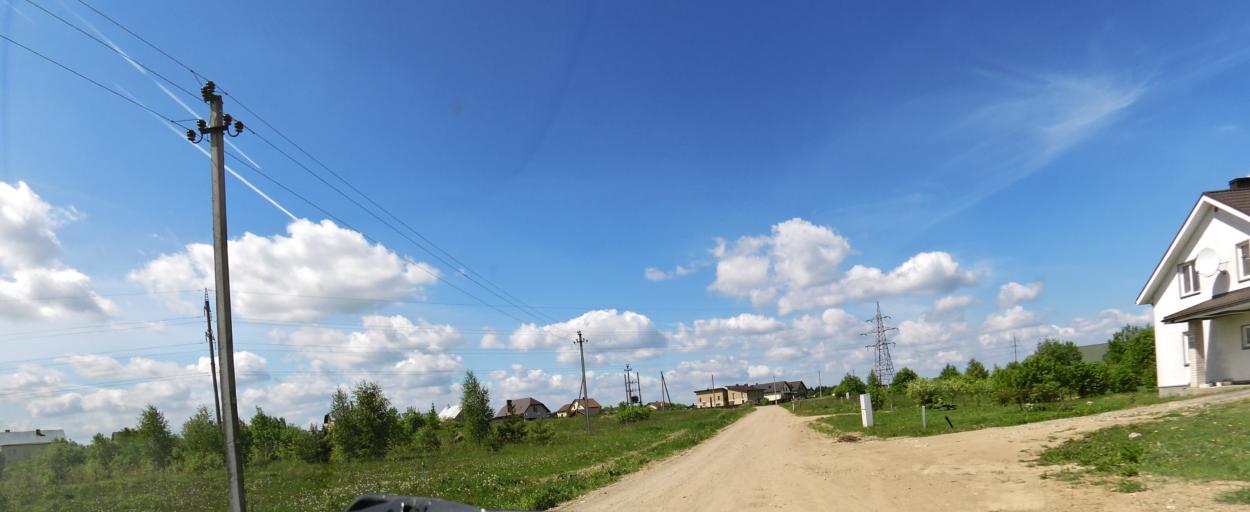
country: LT
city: Lentvaris
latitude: 54.6307
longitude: 25.0927
